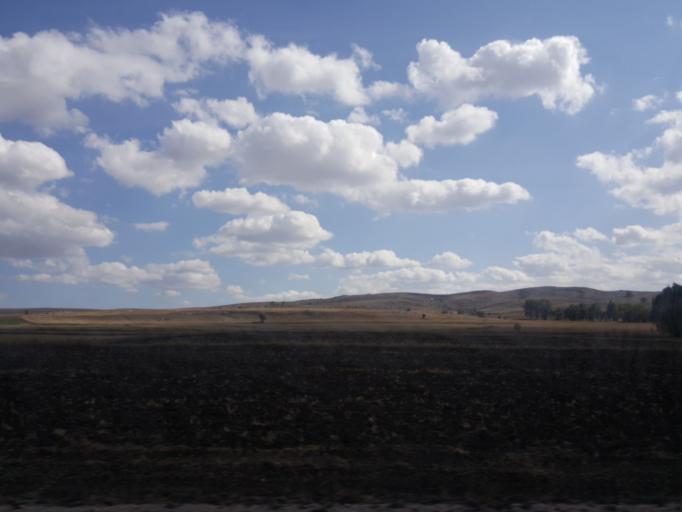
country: TR
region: Tokat
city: Artova
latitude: 40.1501
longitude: 36.3872
